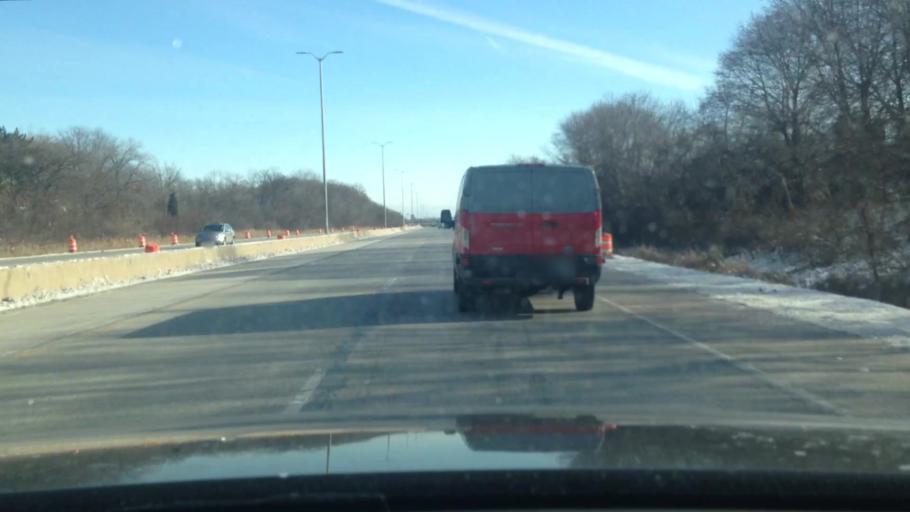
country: US
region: Wisconsin
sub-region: Milwaukee County
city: Hales Corners
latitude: 42.9575
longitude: -88.0686
